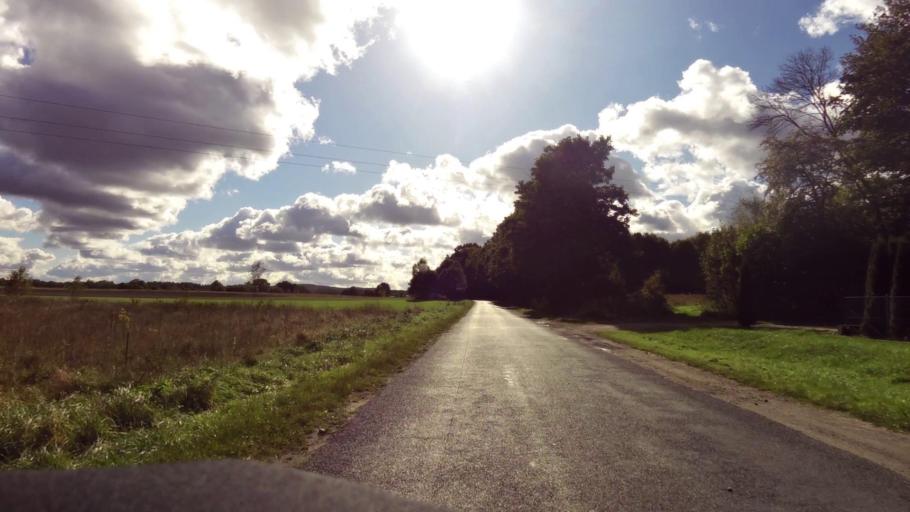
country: PL
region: West Pomeranian Voivodeship
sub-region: Powiat bialogardzki
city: Bialogard
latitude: 53.9977
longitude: 16.0623
